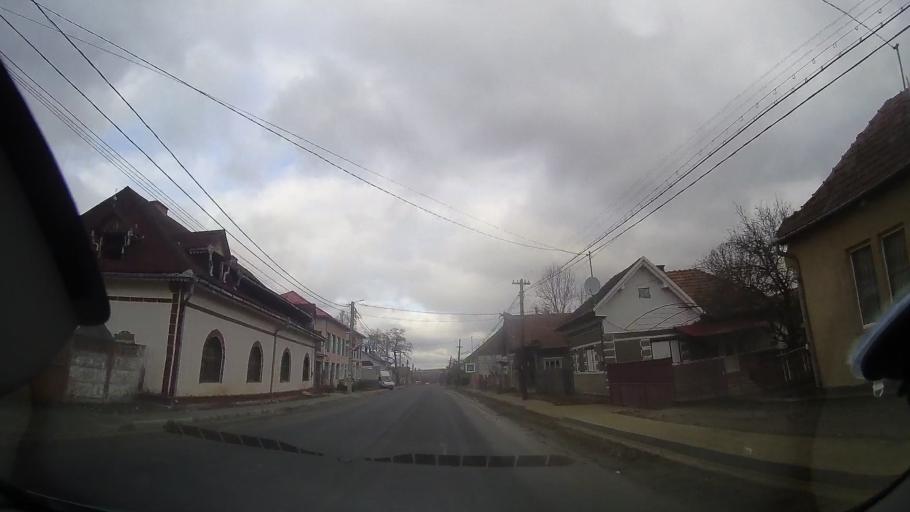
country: RO
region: Cluj
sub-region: Comuna Calatele
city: Calatele
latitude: 46.7653
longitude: 23.0083
